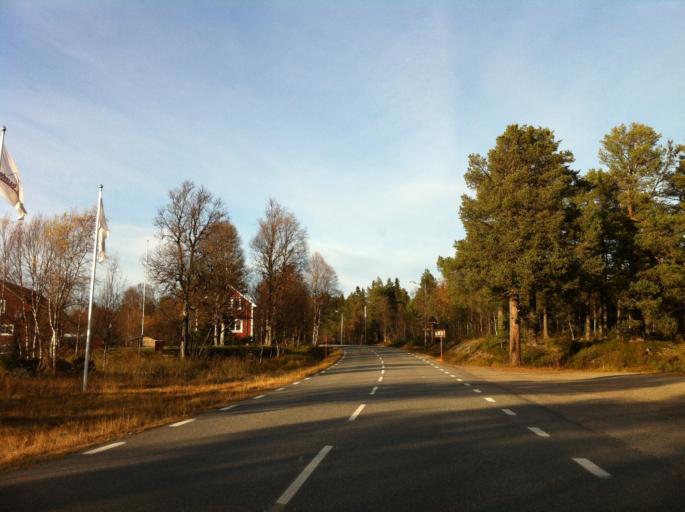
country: NO
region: Hedmark
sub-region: Engerdal
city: Engerdal
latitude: 62.0631
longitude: 12.3182
